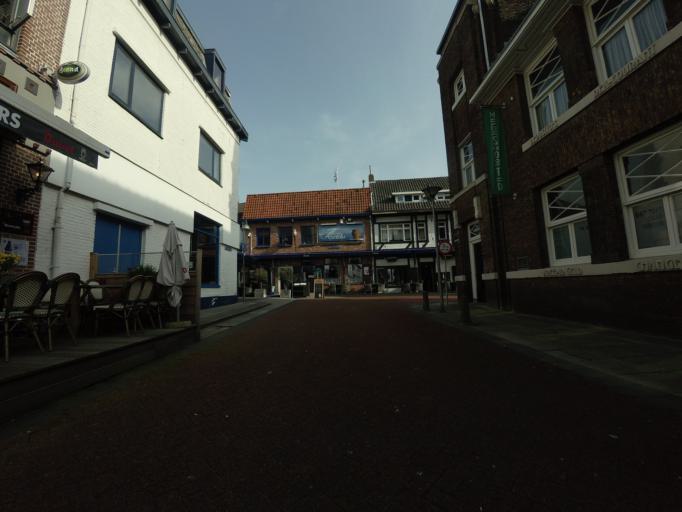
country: NL
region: Zeeland
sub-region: Gemeente Terneuzen
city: Terneuzen
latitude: 51.3378
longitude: 3.8260
